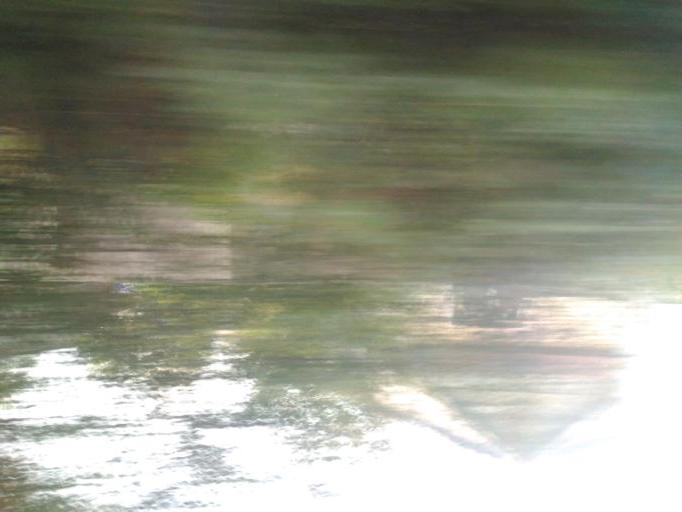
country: RU
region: Ulyanovsk
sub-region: Ulyanovskiy Rayon
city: Ulyanovsk
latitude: 54.2628
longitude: 48.2810
